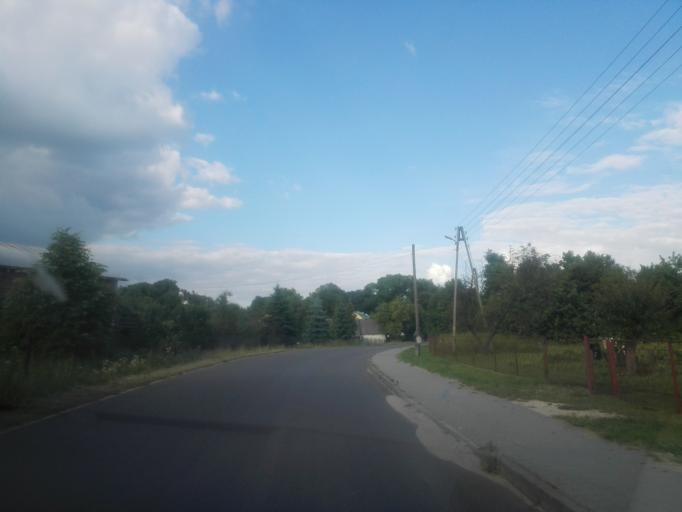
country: PL
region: Swietokrzyskie
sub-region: Powiat jedrzejowski
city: Slupia
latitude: 50.7135
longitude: 19.9807
